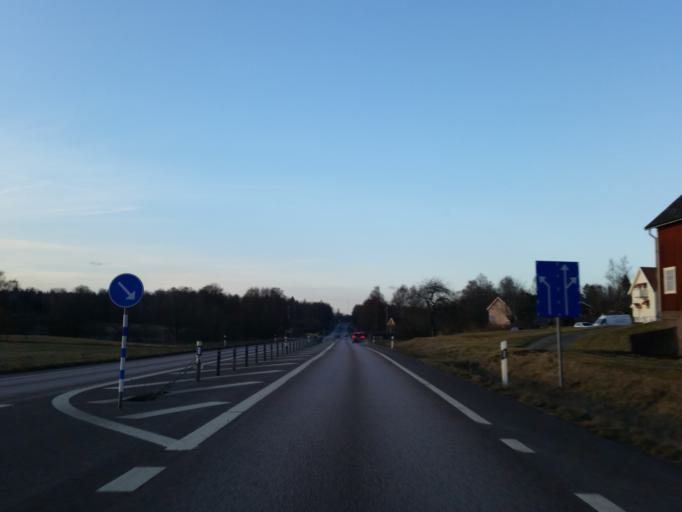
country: SE
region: Kalmar
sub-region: Oskarshamns Kommun
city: Oskarshamn
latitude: 57.4085
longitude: 16.4822
